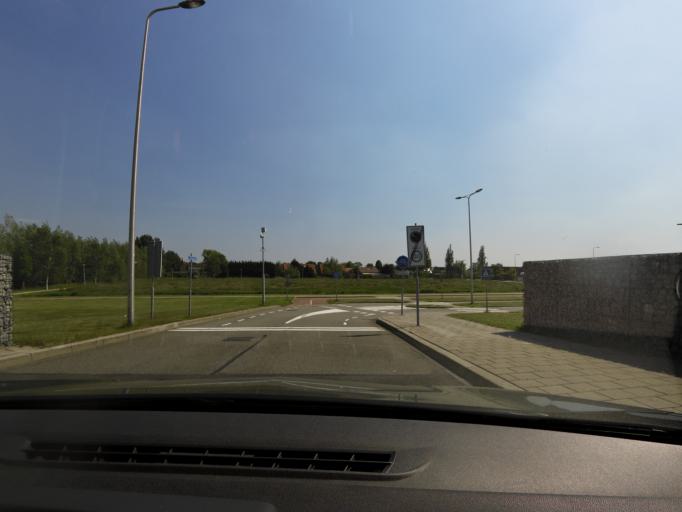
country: NL
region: South Holland
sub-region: Gemeente Lansingerland
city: Berkel en Rodenrijs
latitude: 51.9781
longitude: 4.4545
